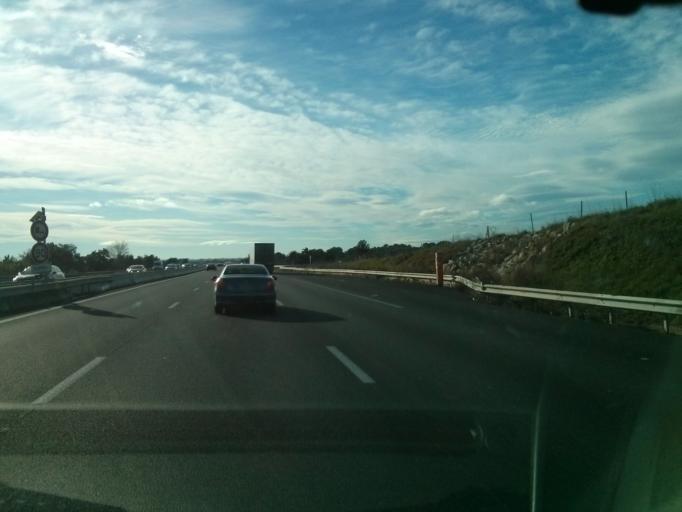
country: FR
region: Languedoc-Roussillon
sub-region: Departement de l'Herault
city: Saint-Genies-des-Mourgues
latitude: 43.6847
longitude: 4.0485
